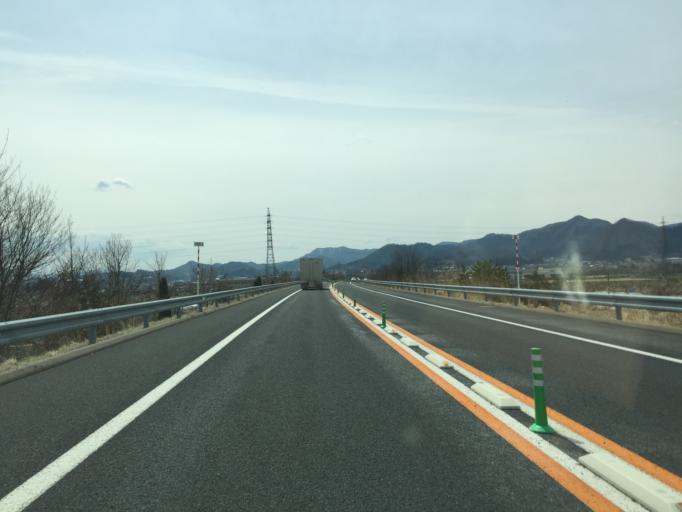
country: JP
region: Yamagata
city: Yamagata-shi
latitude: 38.2568
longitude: 140.2886
